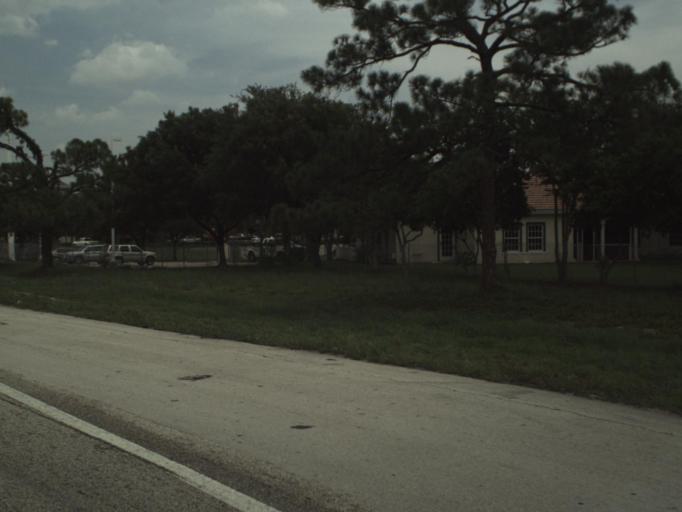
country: US
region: Florida
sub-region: Broward County
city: Tedder
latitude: 26.3001
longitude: -80.1207
